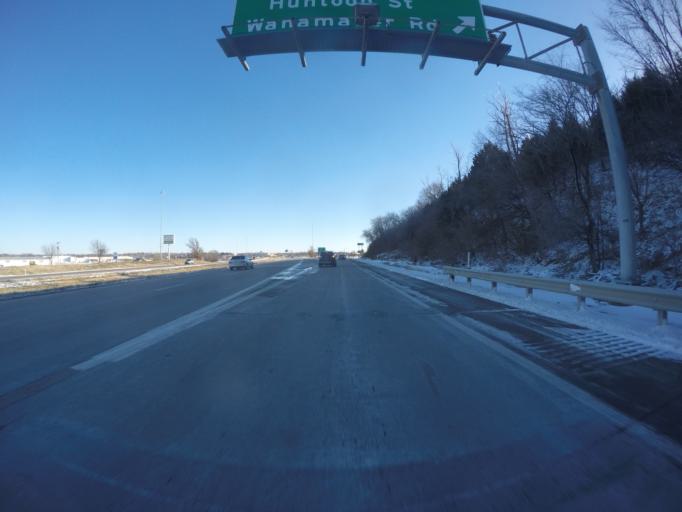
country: US
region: Kansas
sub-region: Shawnee County
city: Topeka
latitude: 39.0458
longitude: -95.7681
